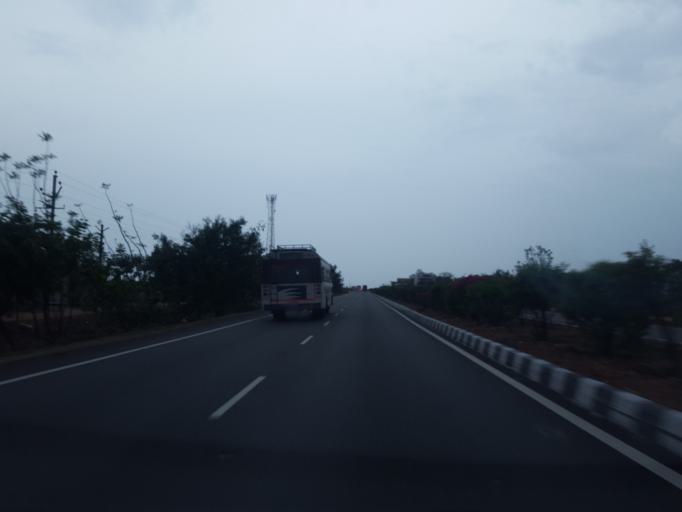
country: IN
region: Telangana
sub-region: Mahbubnagar
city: Farrukhnagar
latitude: 17.1080
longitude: 78.2593
